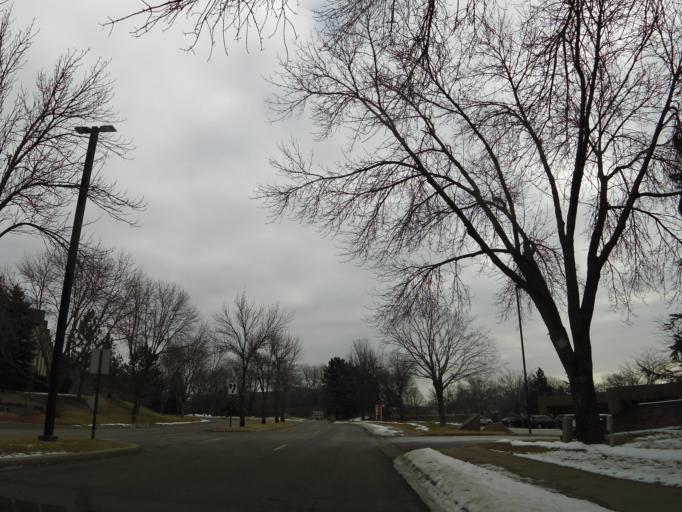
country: US
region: Minnesota
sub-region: Hennepin County
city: Minnetonka Mills
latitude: 44.8850
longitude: -93.4145
